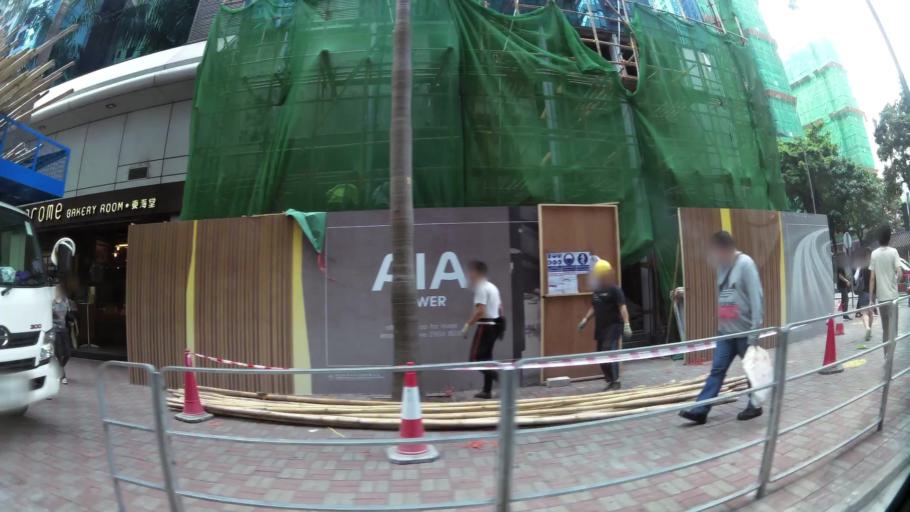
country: HK
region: Wanchai
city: Wan Chai
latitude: 22.2892
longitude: 114.1926
